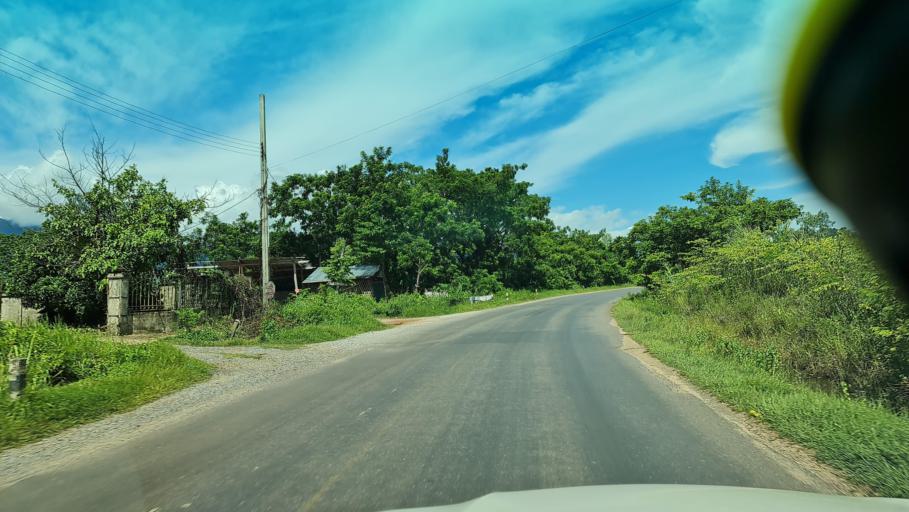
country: LA
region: Bolikhamxai
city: Ban Nahin
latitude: 18.3001
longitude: 104.1276
